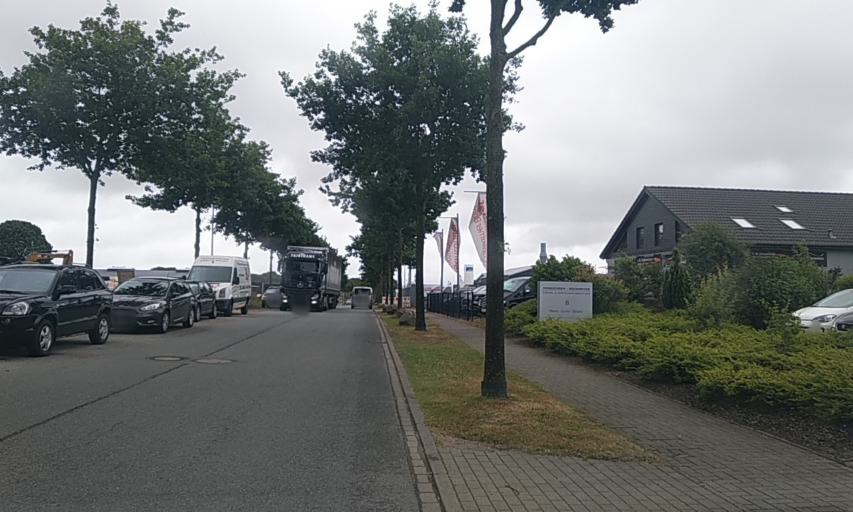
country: DE
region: Schleswig-Holstein
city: Nubel
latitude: 54.5419
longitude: 9.5827
